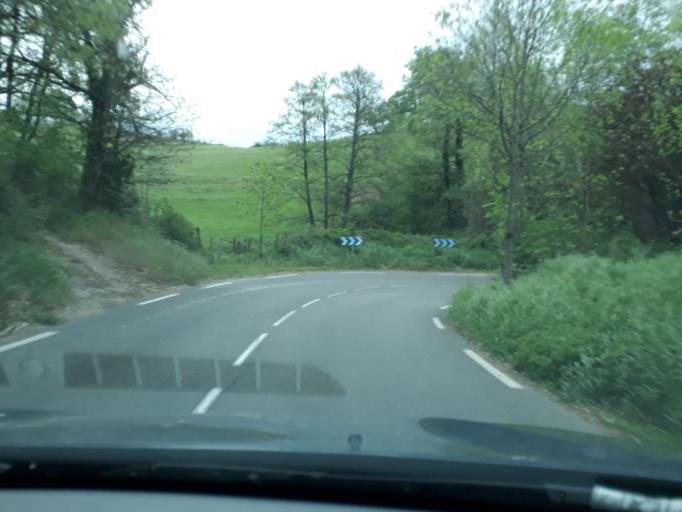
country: FR
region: Rhone-Alpes
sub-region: Departement du Rhone
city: Orlienas
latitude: 45.6761
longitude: 4.7263
